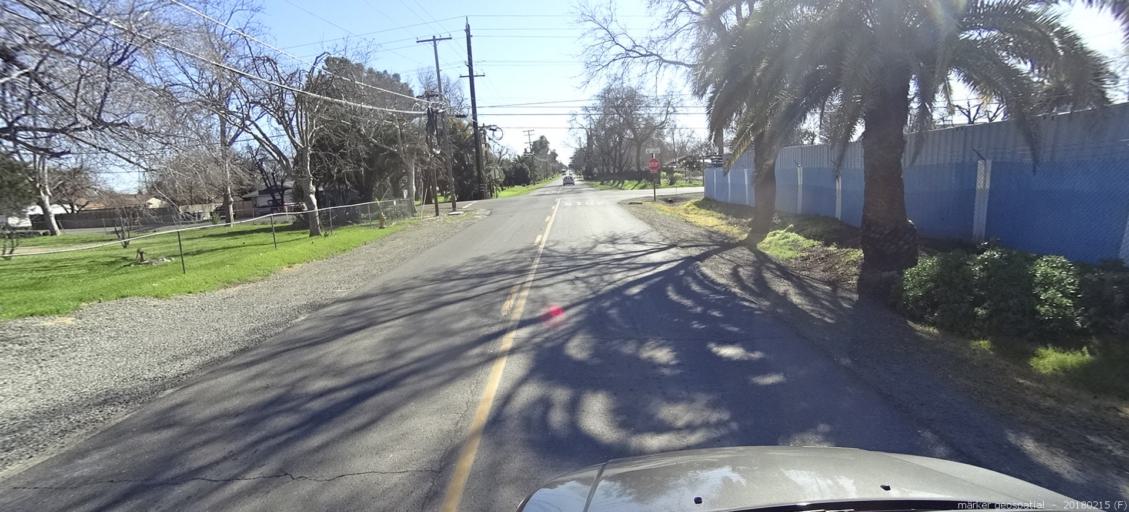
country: US
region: California
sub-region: Sacramento County
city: North Highlands
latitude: 38.6981
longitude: -121.3921
